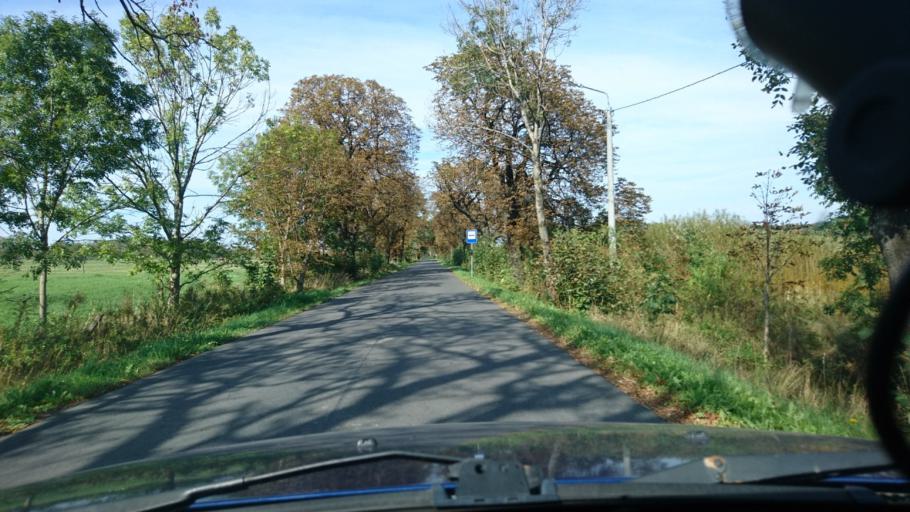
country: PL
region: Silesian Voivodeship
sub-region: Powiat cieszynski
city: Pogorze
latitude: 49.8017
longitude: 18.8793
